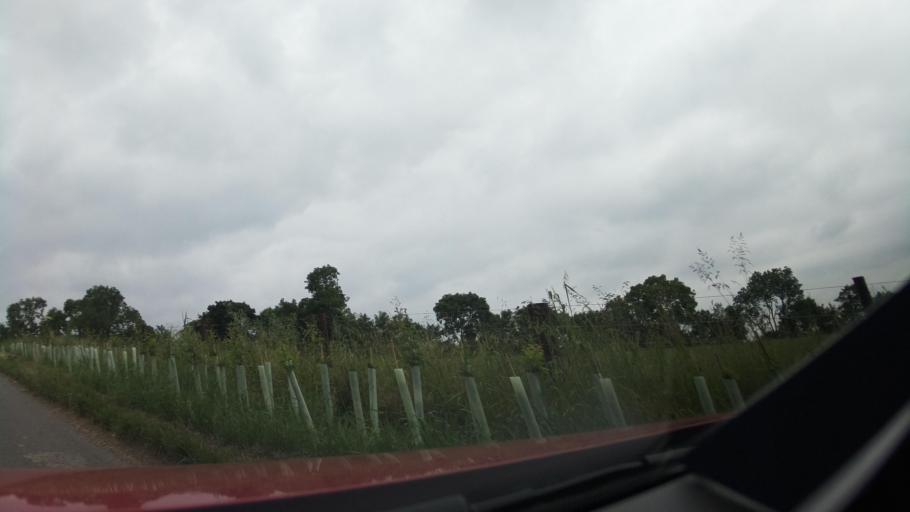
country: GB
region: England
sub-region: District of Rutland
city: Langham
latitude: 52.6797
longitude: -0.7971
